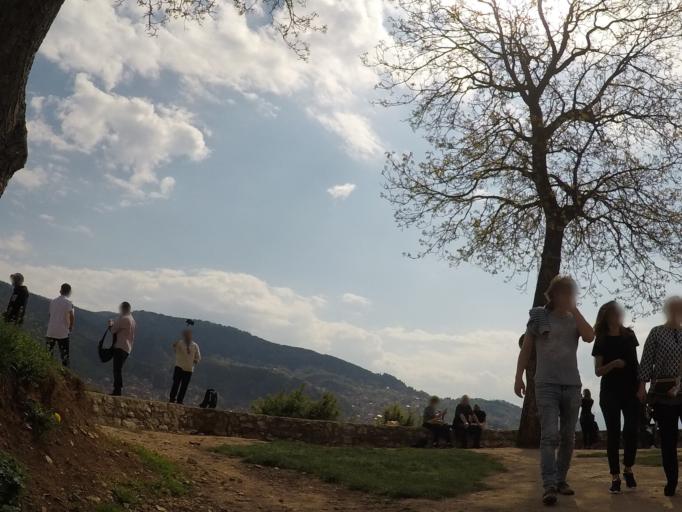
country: BA
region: Federation of Bosnia and Herzegovina
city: Kobilja Glava
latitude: 43.8615
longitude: 18.4378
